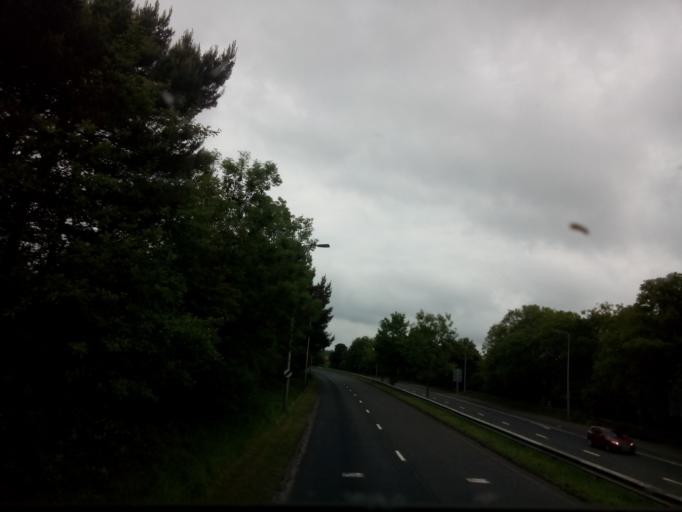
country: GB
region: England
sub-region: County Durham
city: Sacriston
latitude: 54.8115
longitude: -1.5892
